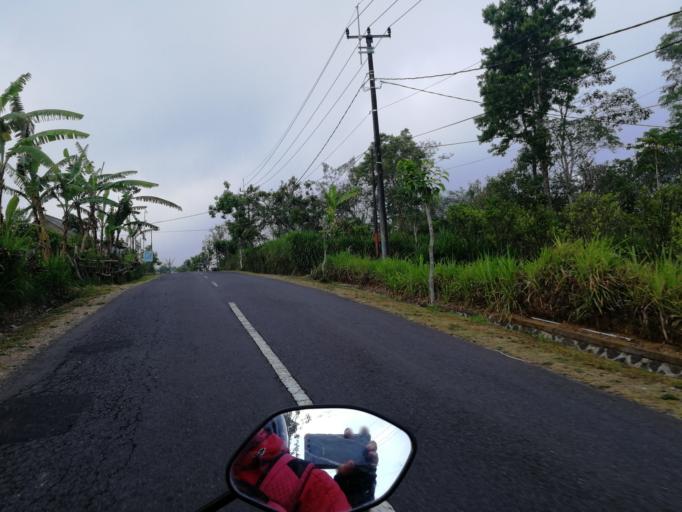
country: ID
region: Bali
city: Banjar Ambengan
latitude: -8.2288
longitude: 115.2447
